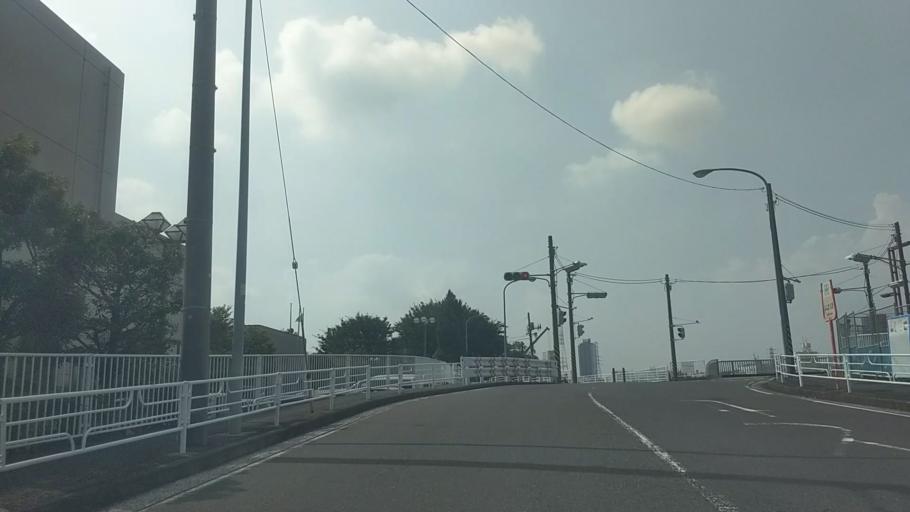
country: JP
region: Kanagawa
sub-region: Kawasaki-shi
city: Kawasaki
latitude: 35.5205
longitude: 139.6775
